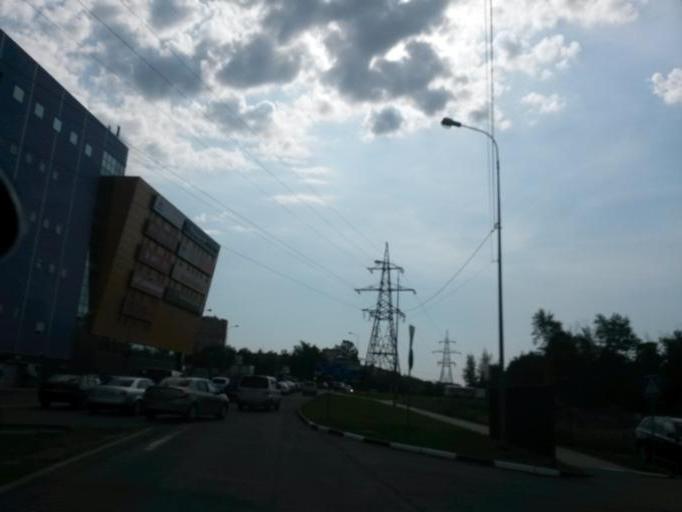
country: RU
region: Moskovskaya
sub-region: Chekhovskiy Rayon
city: Chekhov
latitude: 55.1530
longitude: 37.4583
